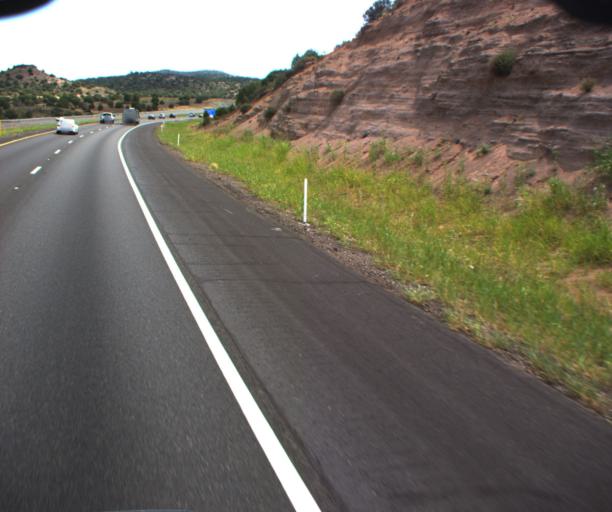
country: US
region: Arizona
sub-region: Yavapai County
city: Camp Verde
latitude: 34.5322
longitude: -111.9781
